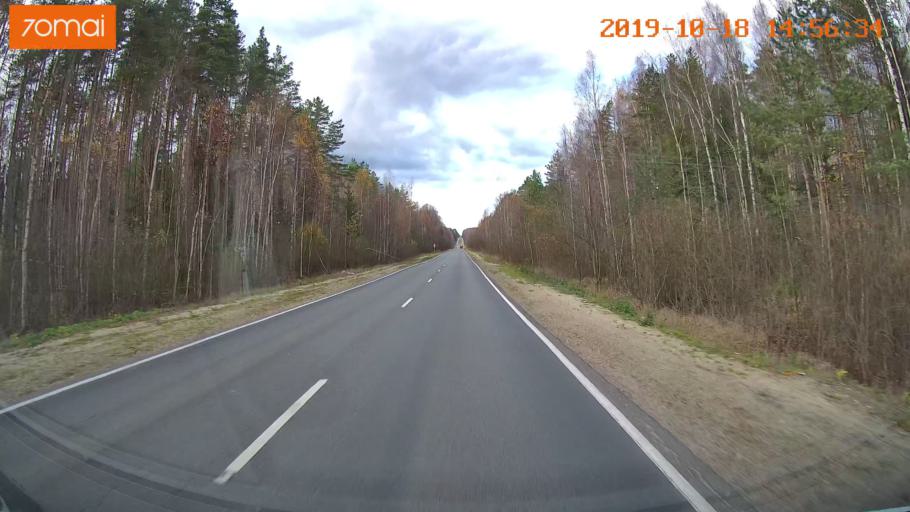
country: RU
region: Vladimir
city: Kurlovo
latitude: 55.4666
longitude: 40.5867
